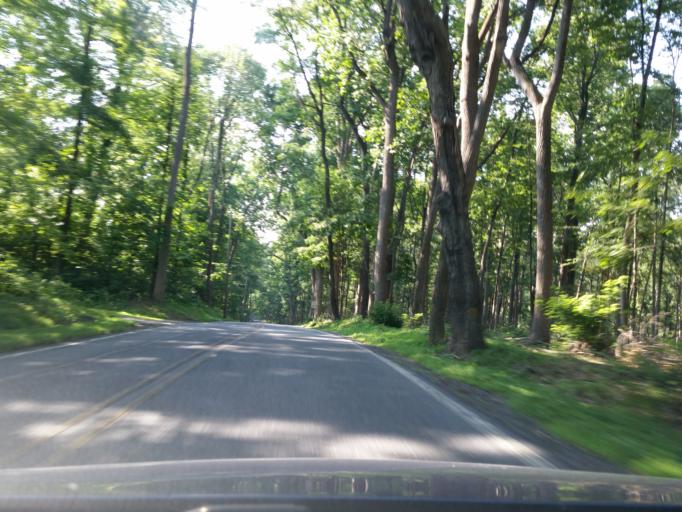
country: US
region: Pennsylvania
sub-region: Lebanon County
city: Campbelltown
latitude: 40.2308
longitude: -76.5049
